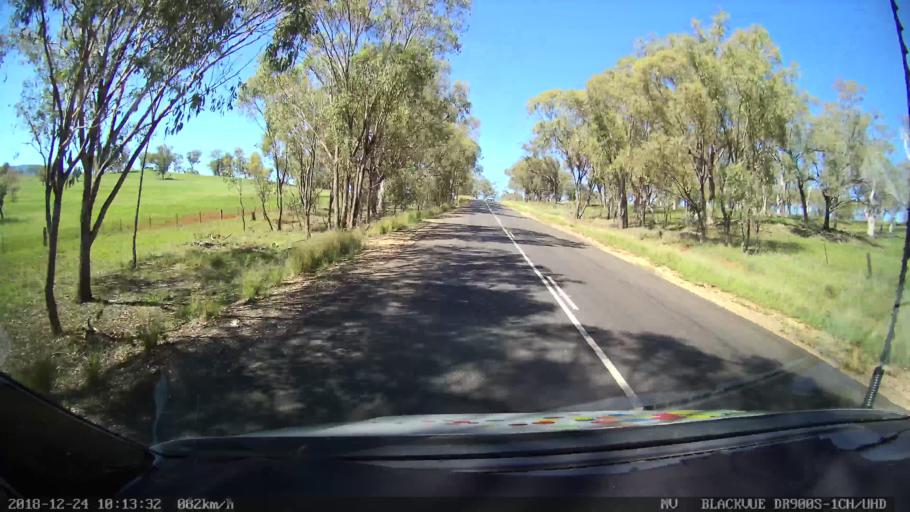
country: AU
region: New South Wales
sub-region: Liverpool Plains
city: Quirindi
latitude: -31.6908
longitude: 150.6391
